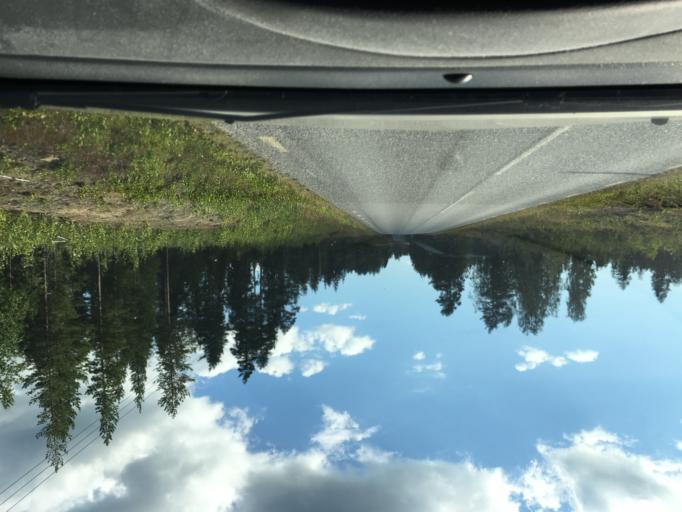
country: SE
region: Norrbotten
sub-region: Kalix Kommun
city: Toere
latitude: 66.0532
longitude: 22.5337
